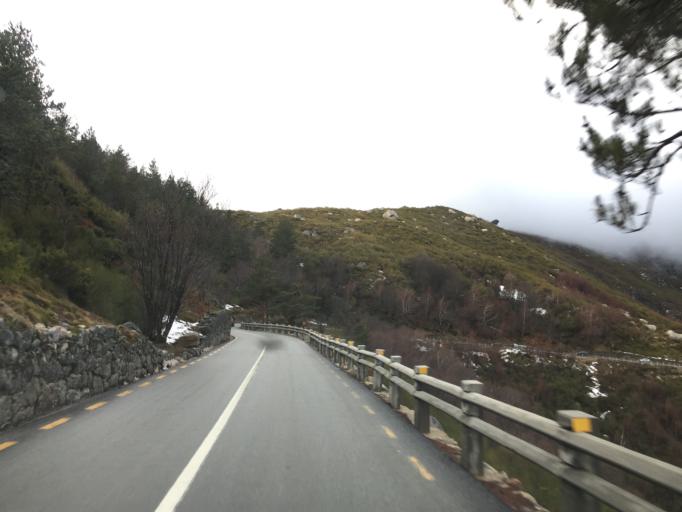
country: PT
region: Castelo Branco
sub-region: Covilha
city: Covilha
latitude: 40.3250
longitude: -7.5748
